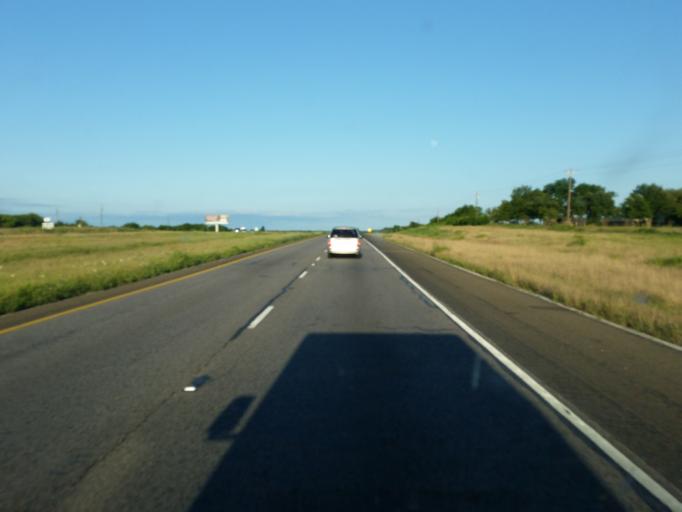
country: US
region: Texas
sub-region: Kaufman County
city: Terrell
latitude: 32.6844
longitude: -96.2092
